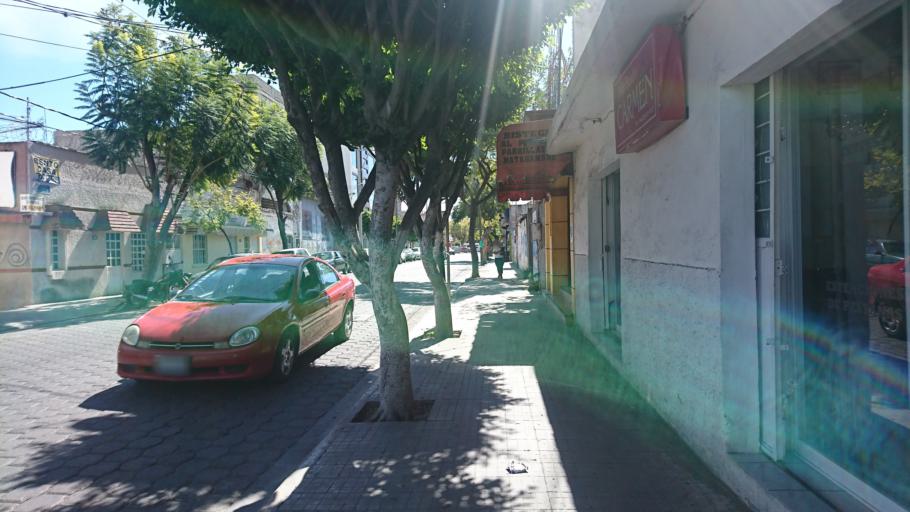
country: MX
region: Puebla
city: Tehuacan
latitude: 18.4683
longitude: -97.3930
